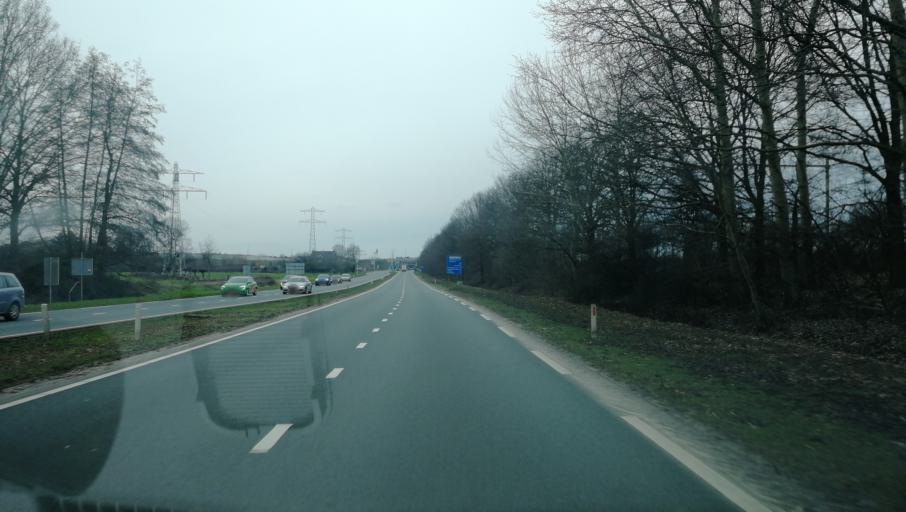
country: NL
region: Limburg
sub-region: Gemeente Venlo
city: Venlo
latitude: 51.3819
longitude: 6.1332
